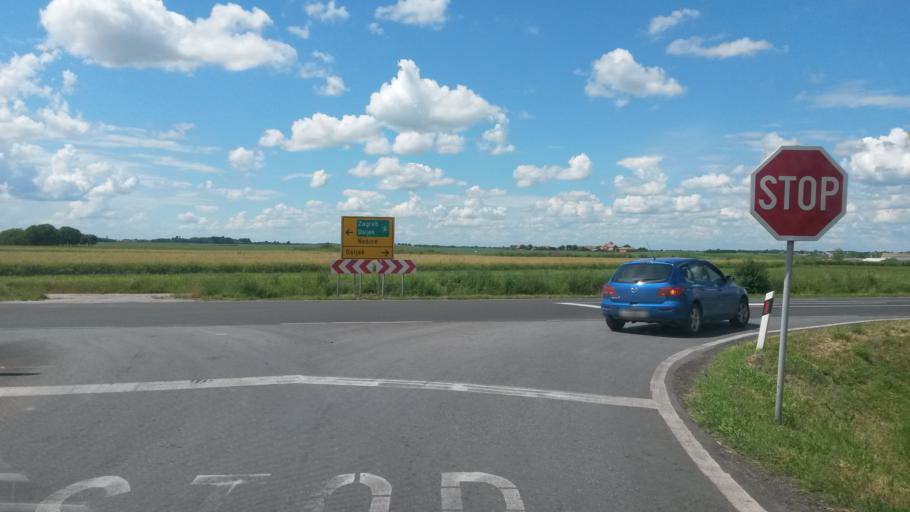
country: HR
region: Osjecko-Baranjska
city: Viskovci
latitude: 45.3354
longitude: 18.4194
